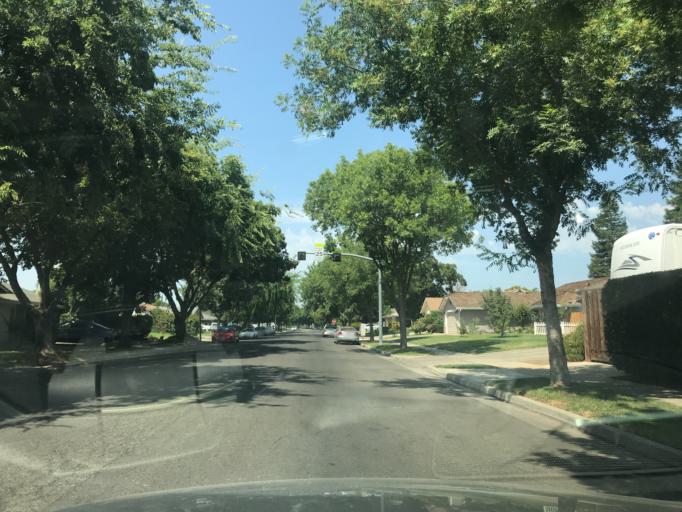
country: US
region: California
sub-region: Merced County
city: Merced
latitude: 37.3285
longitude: -120.4584
